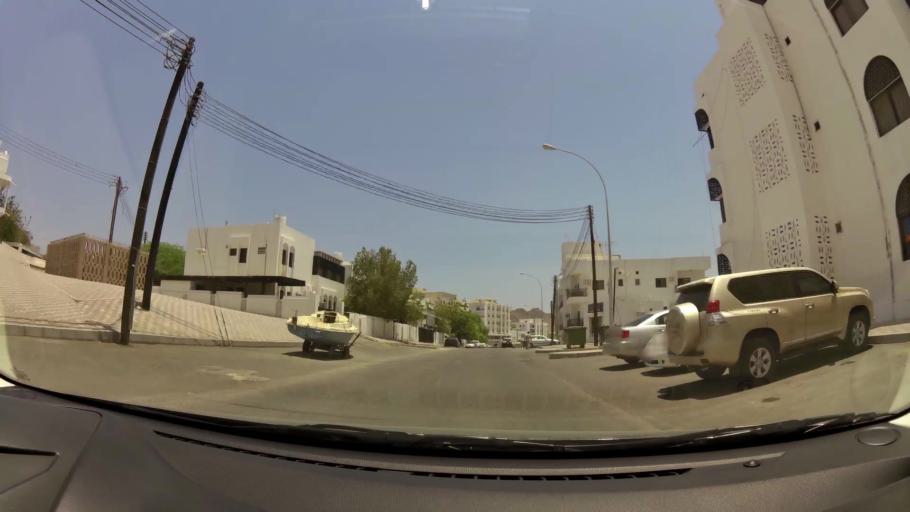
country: OM
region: Muhafazat Masqat
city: Muscat
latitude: 23.6116
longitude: 58.5432
